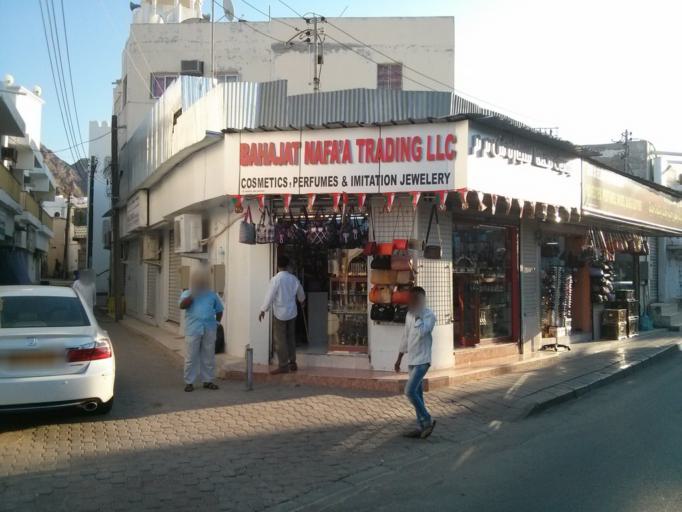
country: OM
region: Muhafazat Masqat
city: Muscat
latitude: 23.6186
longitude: 58.5635
